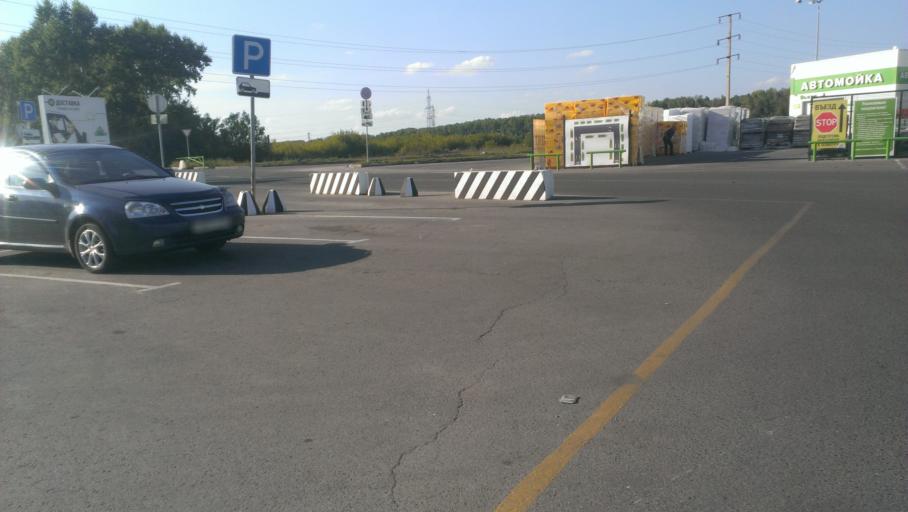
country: RU
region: Altai Krai
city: Novosilikatnyy
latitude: 53.3495
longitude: 83.6308
